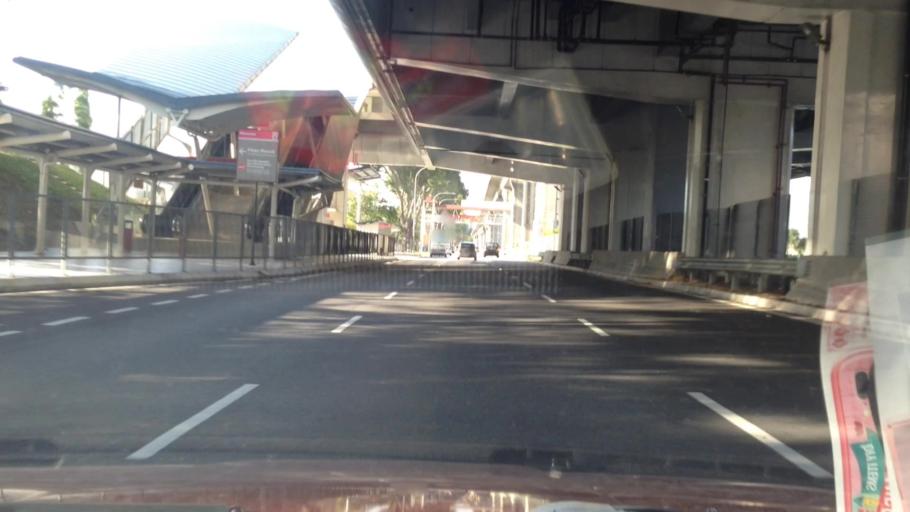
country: MY
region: Selangor
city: Subang Jaya
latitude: 3.0347
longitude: 101.5881
